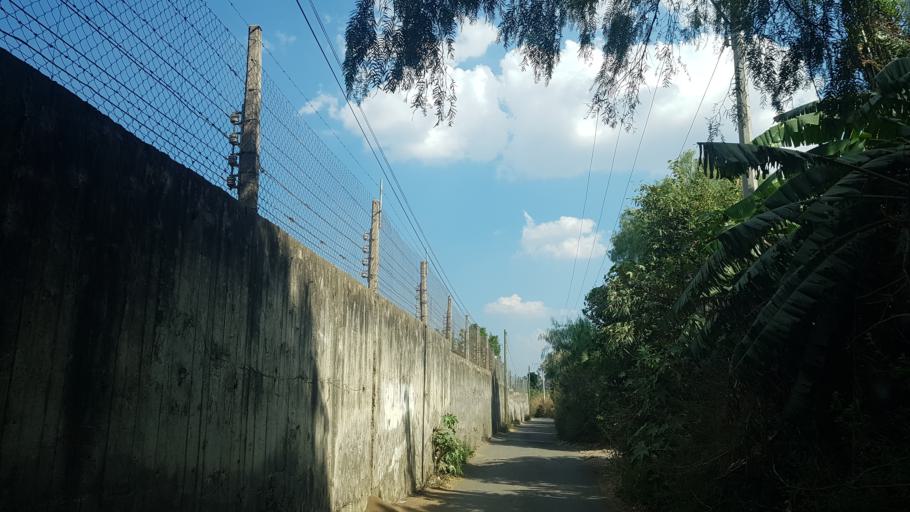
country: MX
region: Puebla
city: Atlixco
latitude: 18.8741
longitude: -98.4861
